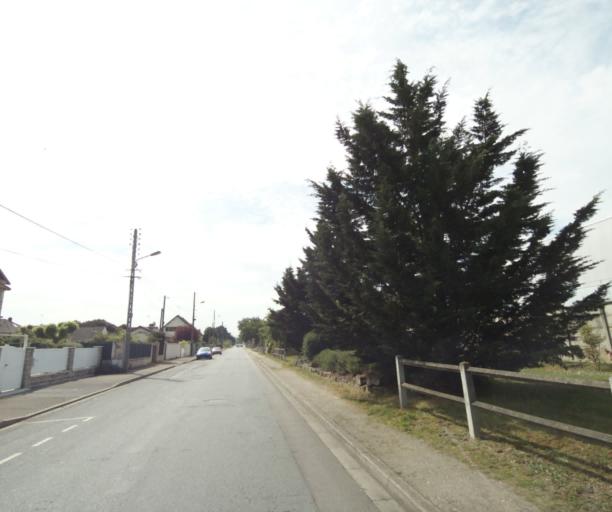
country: FR
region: Ile-de-France
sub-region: Departement des Yvelines
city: Mezy-sur-Seine
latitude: 48.9937
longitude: 1.8954
